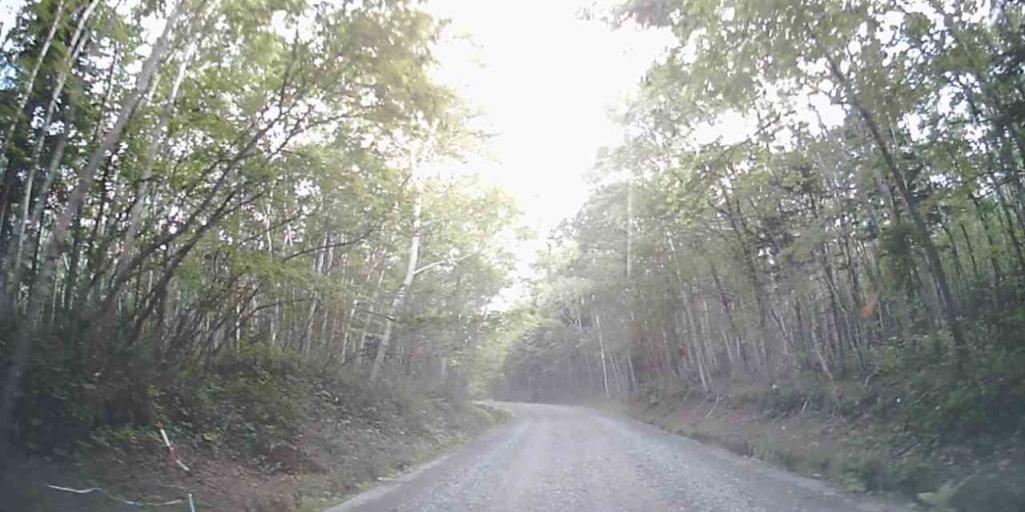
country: JP
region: Hokkaido
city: Shiraoi
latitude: 42.7100
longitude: 141.3989
